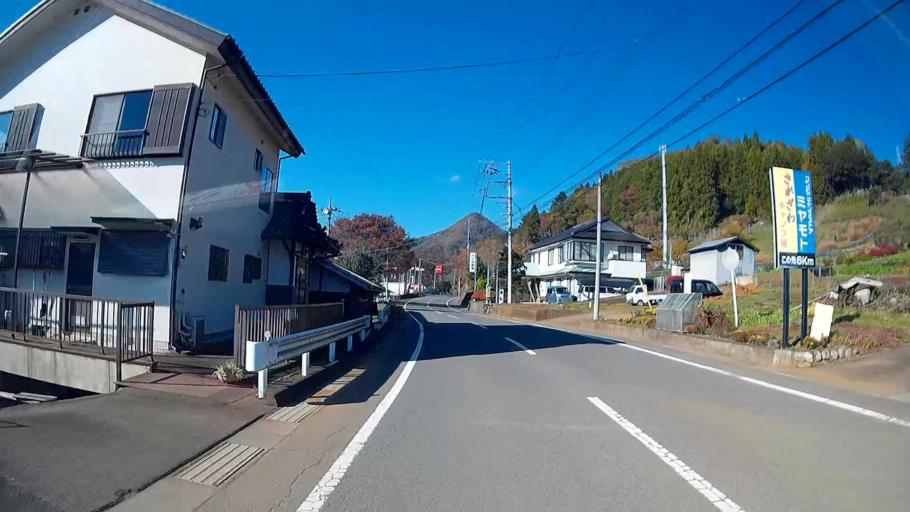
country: JP
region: Yamanashi
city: Uenohara
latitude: 35.5825
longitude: 139.1220
